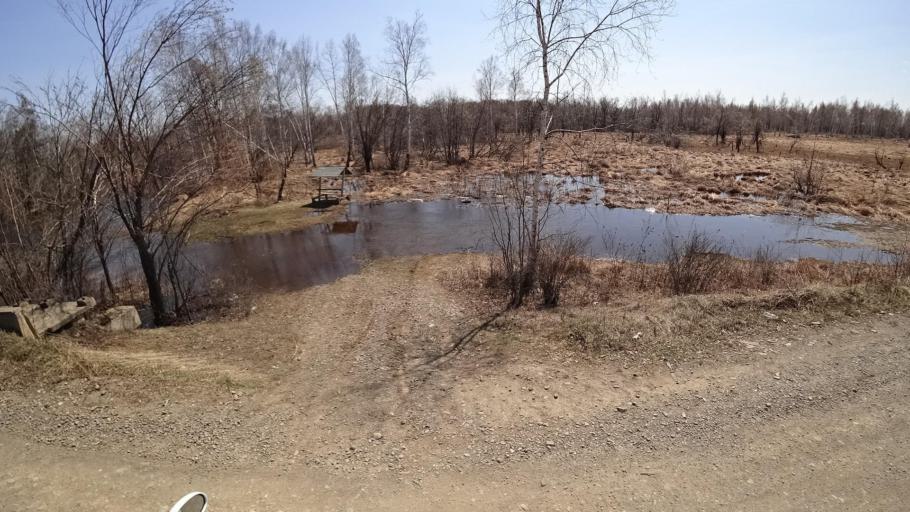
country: RU
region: Khabarovsk Krai
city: Khurba
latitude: 50.4194
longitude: 136.8299
